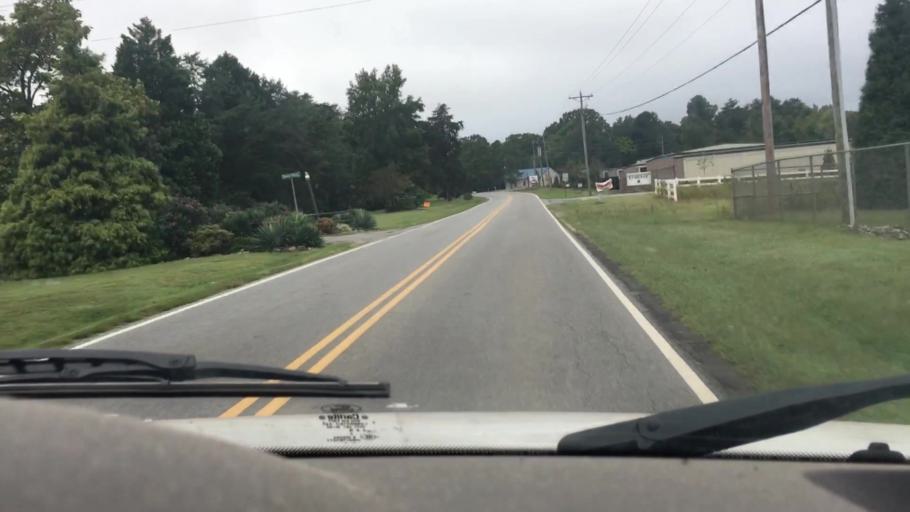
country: US
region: North Carolina
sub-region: Lincoln County
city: Denver
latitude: 35.5396
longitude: -81.0187
